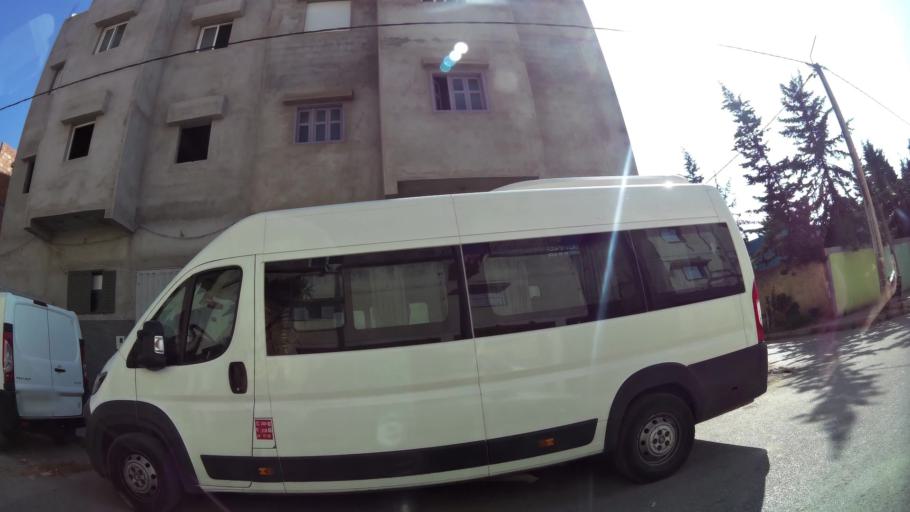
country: MA
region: Rabat-Sale-Zemmour-Zaer
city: Sale
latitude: 34.0569
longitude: -6.7729
